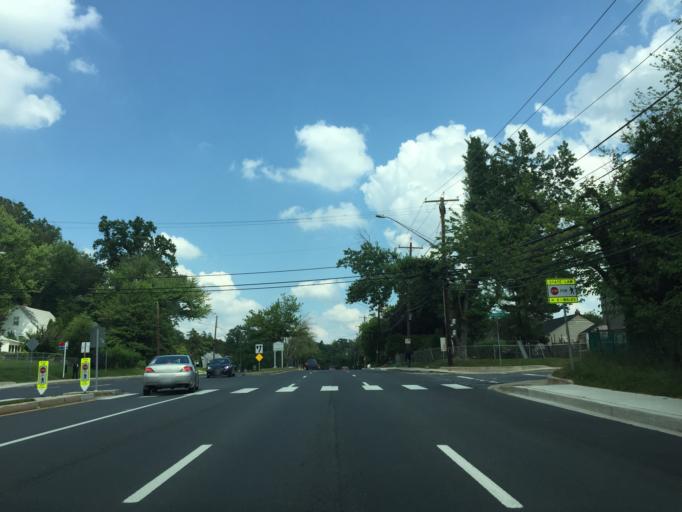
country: US
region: Maryland
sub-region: Montgomery County
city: Glenmont
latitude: 39.0583
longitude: -77.0558
